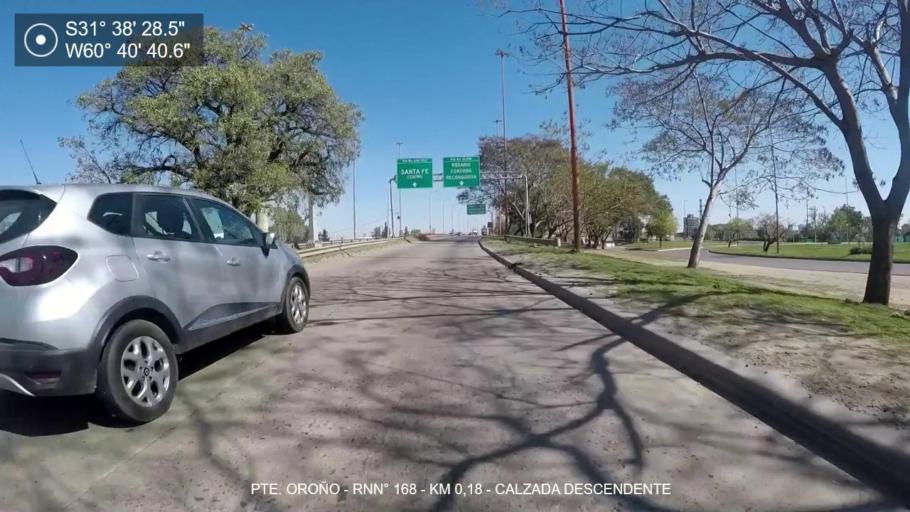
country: AR
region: Santa Fe
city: Santa Fe de la Vera Cruz
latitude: -31.6413
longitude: -60.6777
